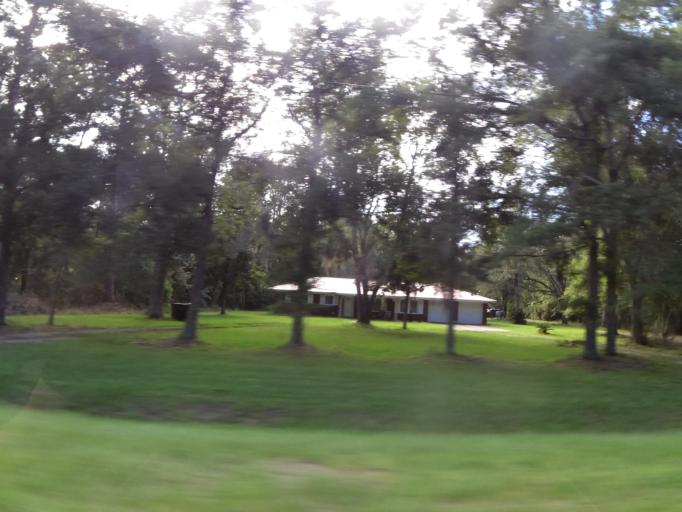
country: US
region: Georgia
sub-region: Glynn County
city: Country Club Estates
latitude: 31.2538
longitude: -81.4434
